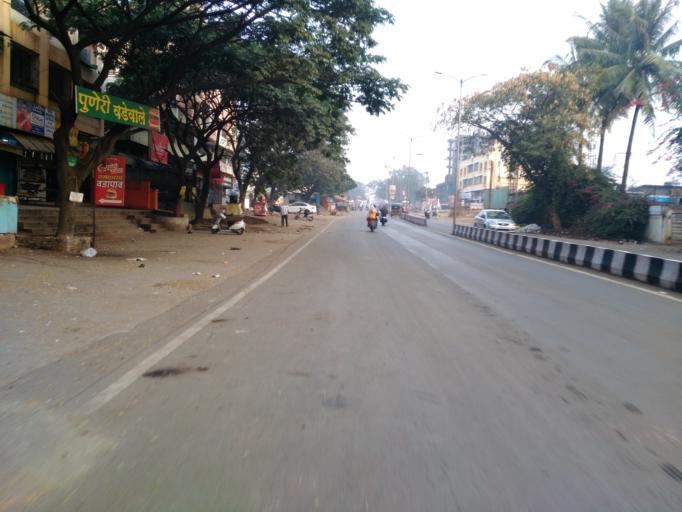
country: IN
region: Maharashtra
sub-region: Pune Division
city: Pune
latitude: 18.4559
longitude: 73.8906
